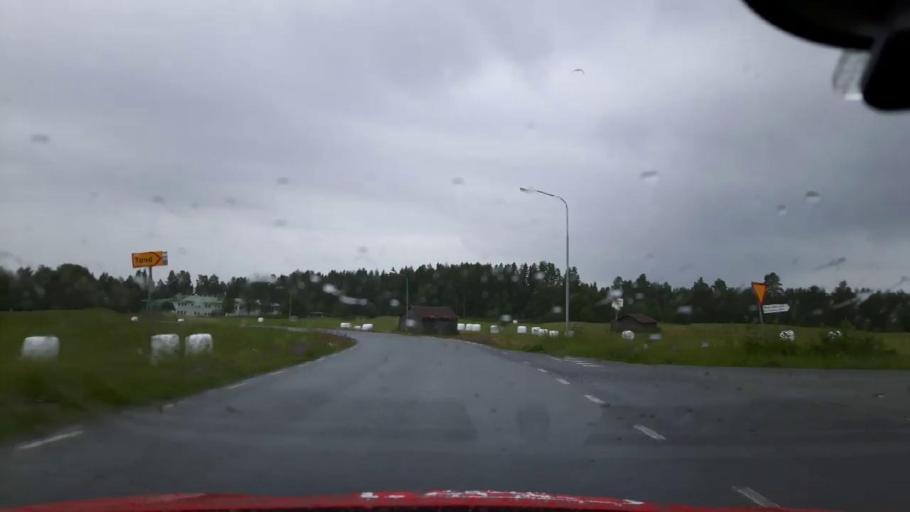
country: SE
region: Jaemtland
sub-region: OEstersunds Kommun
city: Brunflo
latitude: 63.0075
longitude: 14.7304
